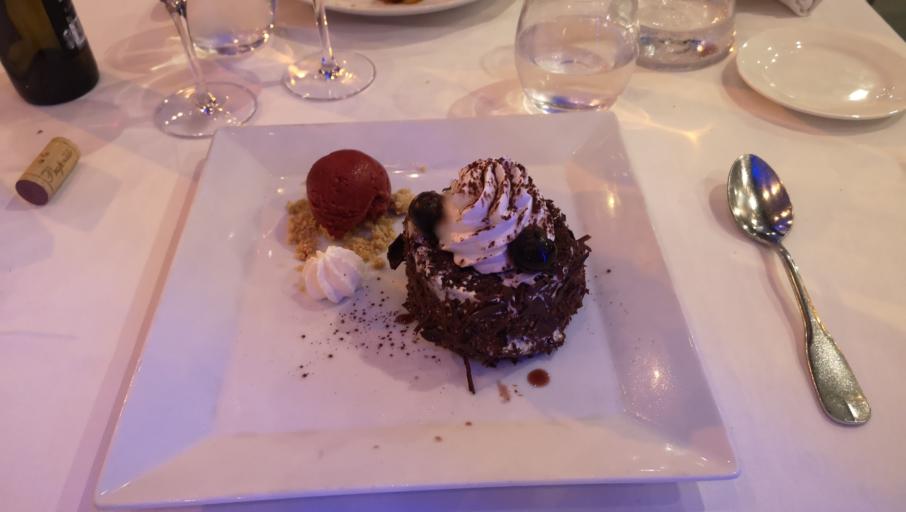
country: FR
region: Languedoc-Roussillon
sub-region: Departement des Pyrenees-Orientales
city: Banyuls de la Marenda
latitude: 42.4871
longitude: 3.1271
